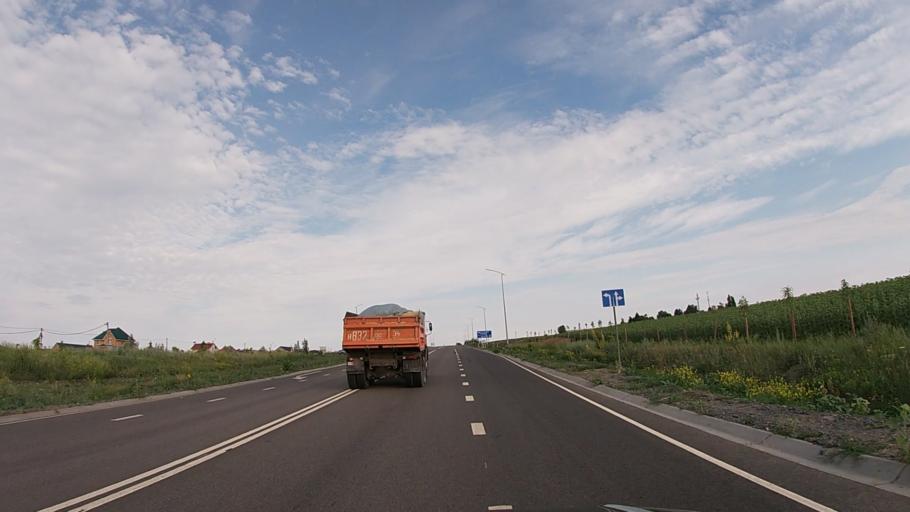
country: RU
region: Belgorod
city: Severnyy
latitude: 50.6714
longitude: 36.4824
